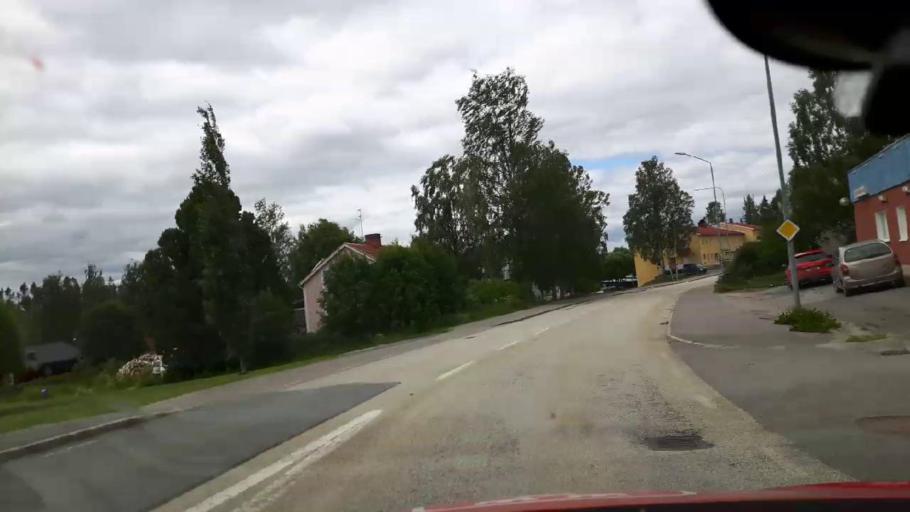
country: SE
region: Jaemtland
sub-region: Braecke Kommun
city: Braecke
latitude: 62.9127
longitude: 15.2321
